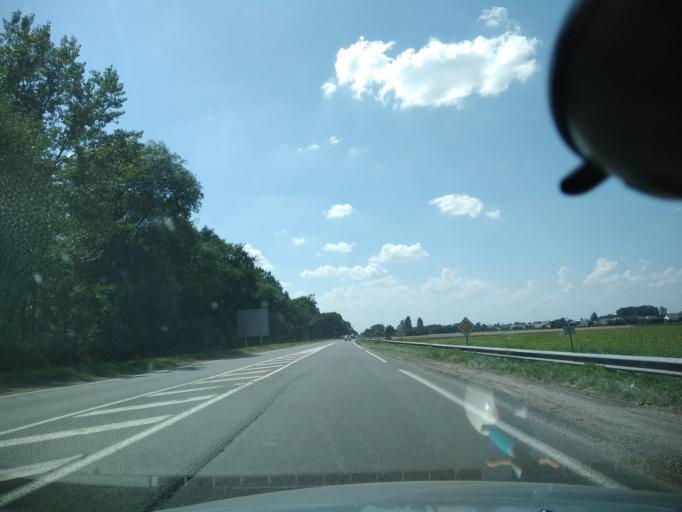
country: FR
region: Centre
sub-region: Departement d'Indre-et-Loire
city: Larcay
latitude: 47.3813
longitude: 0.7820
